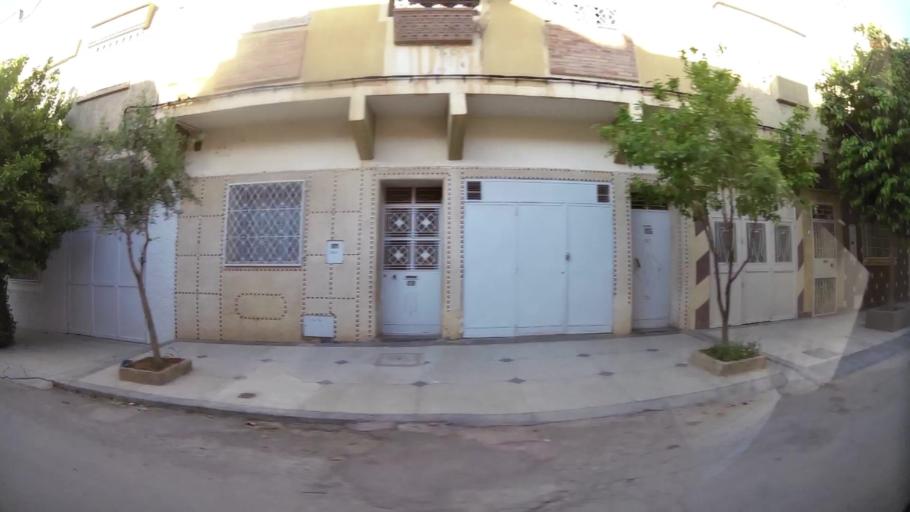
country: MA
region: Oriental
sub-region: Oujda-Angad
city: Oujda
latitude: 34.6980
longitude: -1.9056
